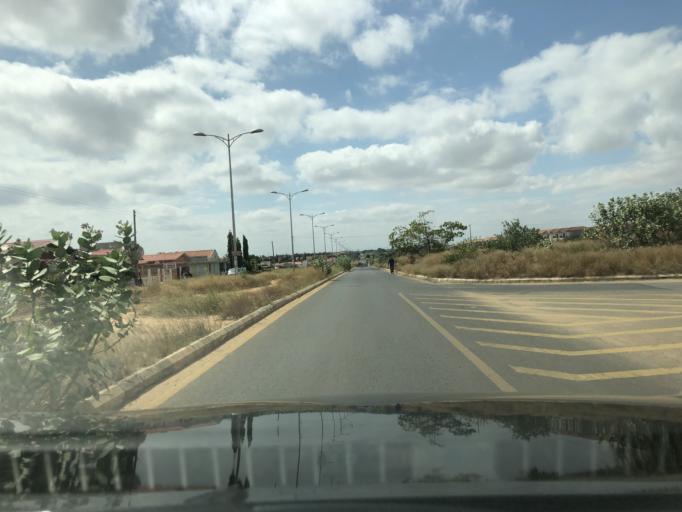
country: AO
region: Luanda
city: Luanda
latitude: -8.9456
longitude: 13.2447
